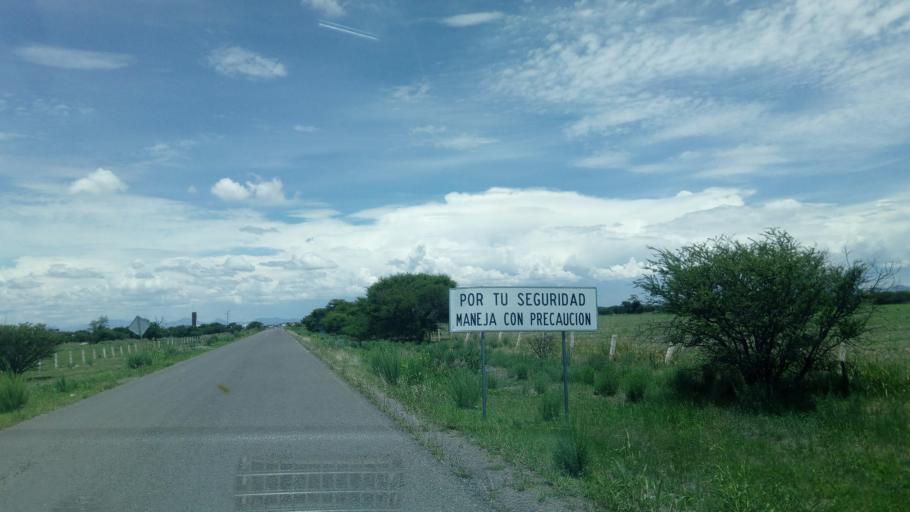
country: MX
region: Durango
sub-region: Durango
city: Jose Refugio Salcido
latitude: 24.1581
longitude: -104.5075
